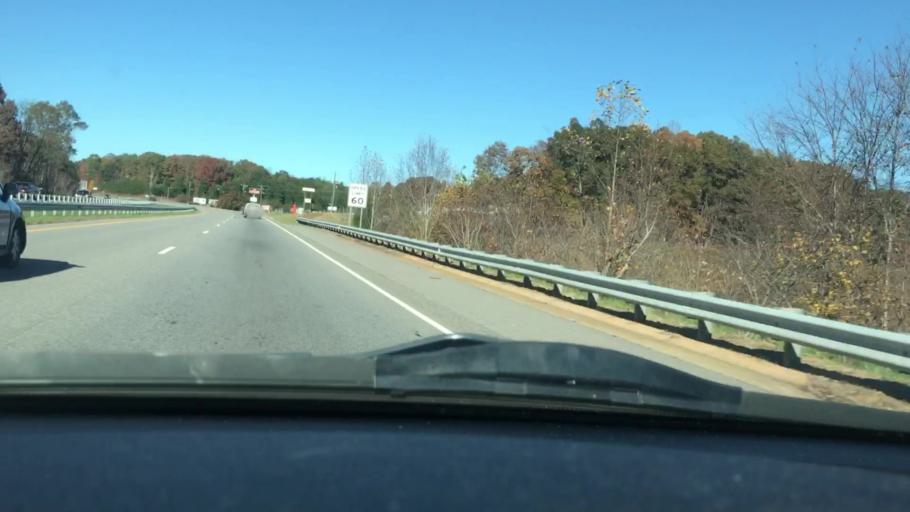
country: US
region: North Carolina
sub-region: Rockingham County
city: Stoneville
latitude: 36.4765
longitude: -79.9247
